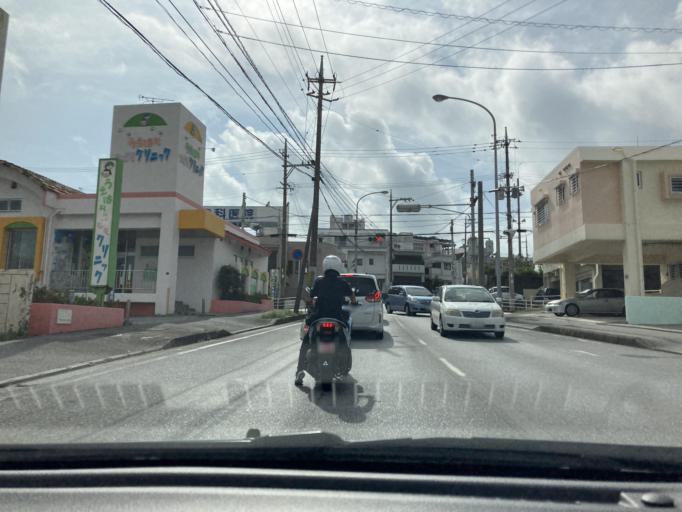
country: JP
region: Okinawa
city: Ginowan
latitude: 26.2614
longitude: 127.7632
